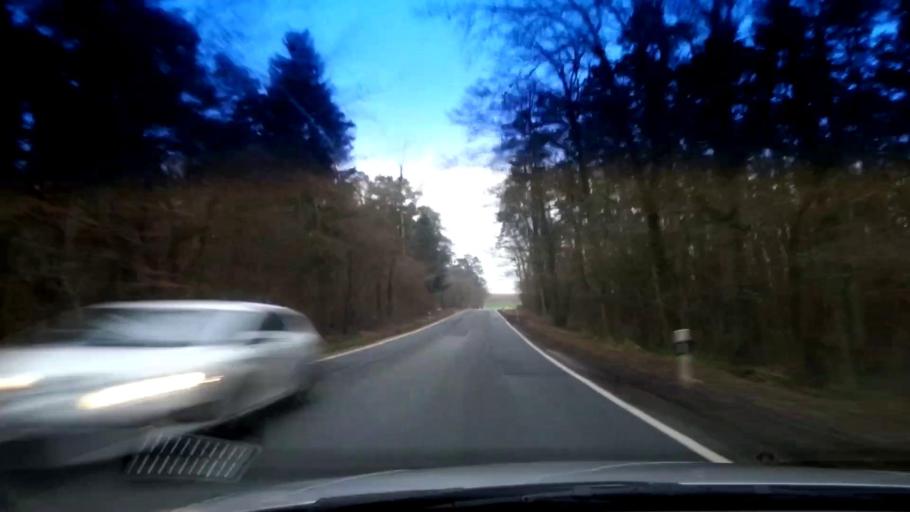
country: DE
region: Bavaria
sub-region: Upper Franconia
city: Burgebrach
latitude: 49.8094
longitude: 10.7840
